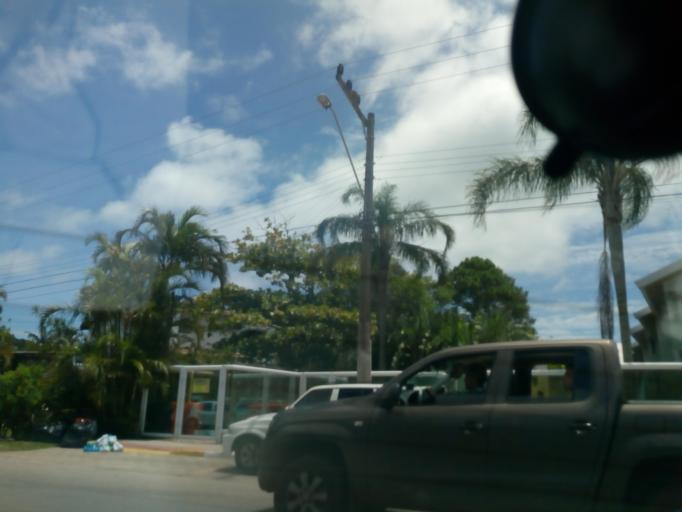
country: BR
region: Santa Catarina
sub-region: Florianopolis
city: Itacorubi
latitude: -27.3907
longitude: -48.4254
